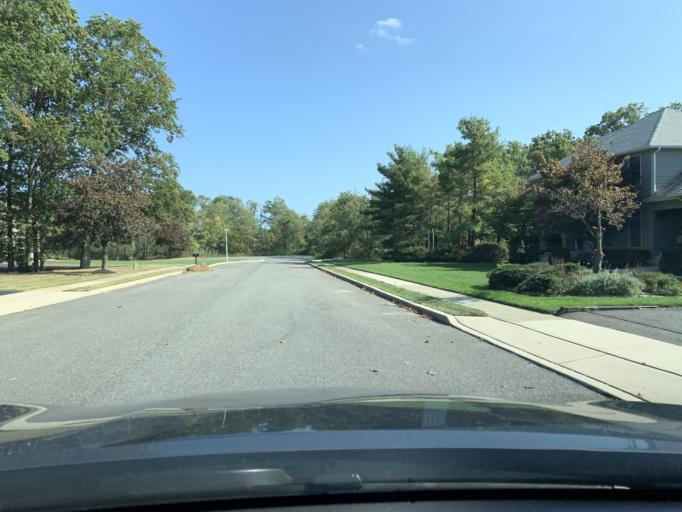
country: US
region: New Jersey
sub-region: Monmouth County
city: Shrewsbury
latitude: 40.3153
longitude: -74.0528
